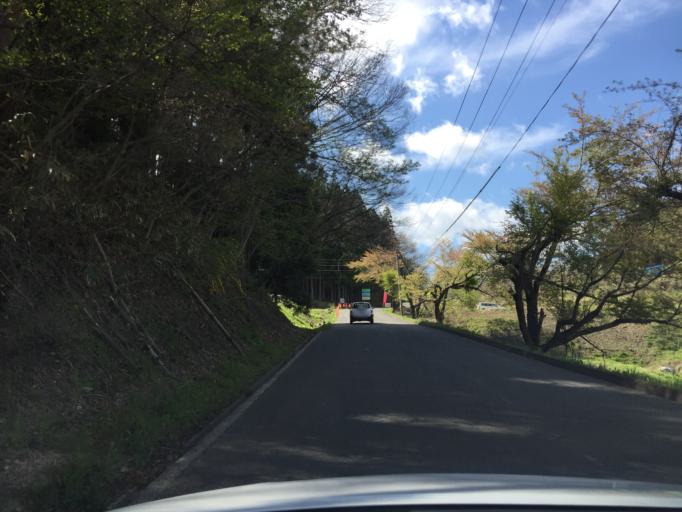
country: JP
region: Fukushima
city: Funehikimachi-funehiki
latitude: 37.5747
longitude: 140.6932
